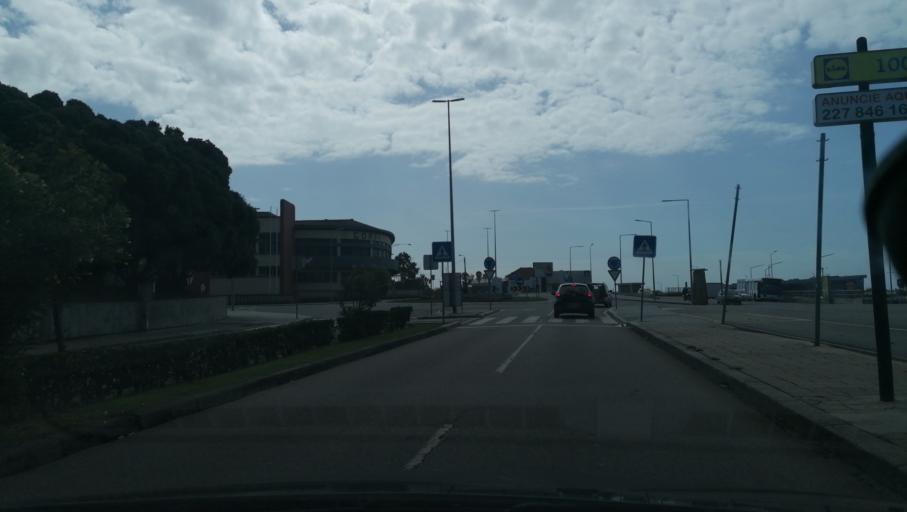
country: PT
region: Aveiro
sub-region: Espinho
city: Espinho
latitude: 41.0015
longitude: -8.6382
